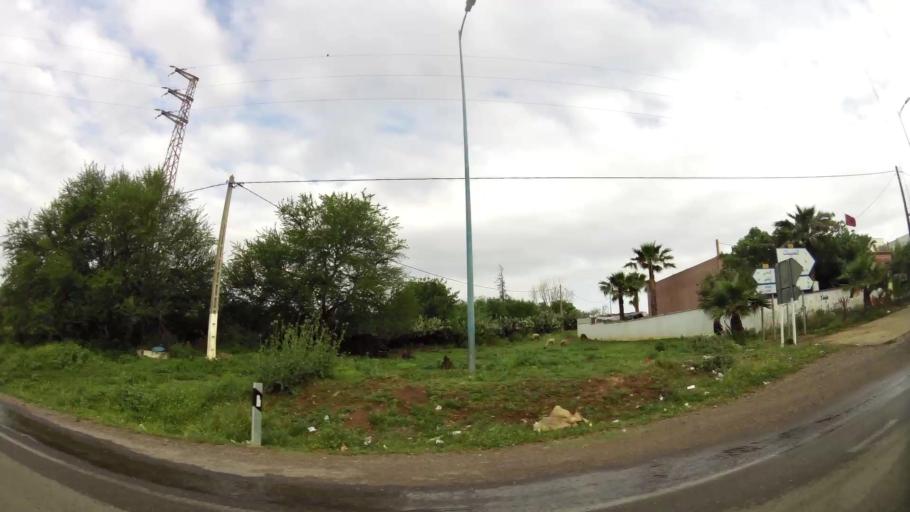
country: MA
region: Rabat-Sale-Zemmour-Zaer
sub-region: Khemisset
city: Khemisset
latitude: 33.7833
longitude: -6.1281
